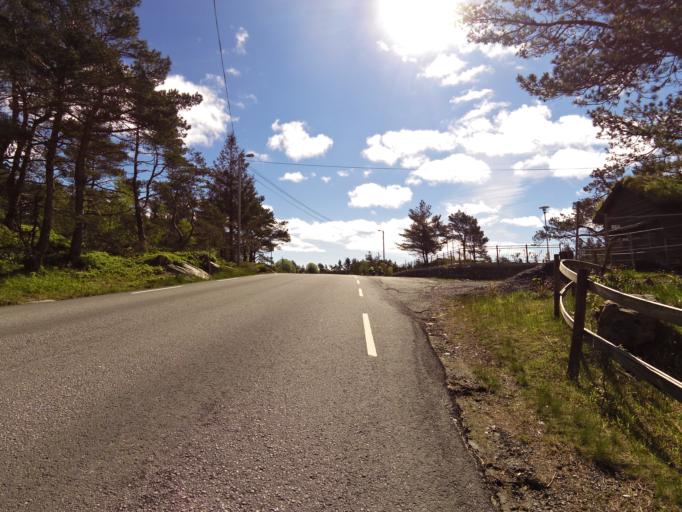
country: NO
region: Hordaland
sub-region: Os
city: Hagavik
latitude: 60.2571
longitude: 5.3618
